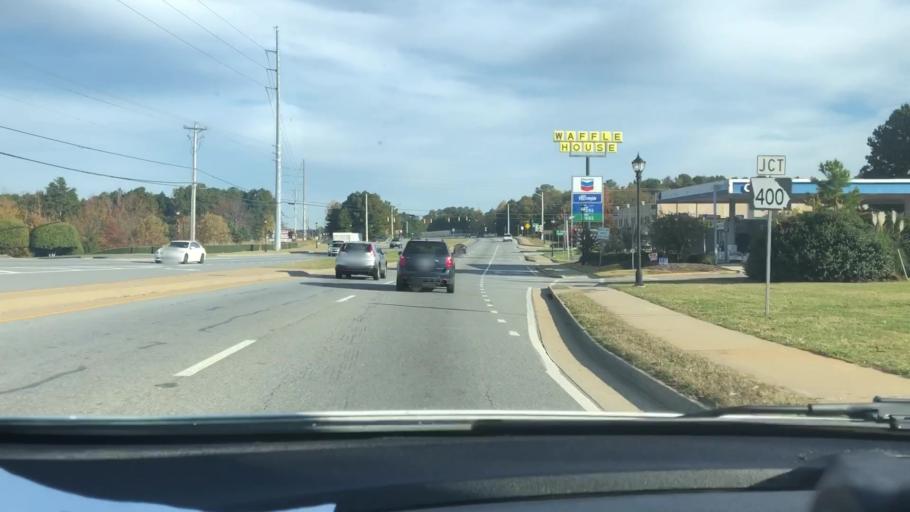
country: US
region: Georgia
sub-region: Forsyth County
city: Cumming
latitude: 34.1544
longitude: -84.1739
